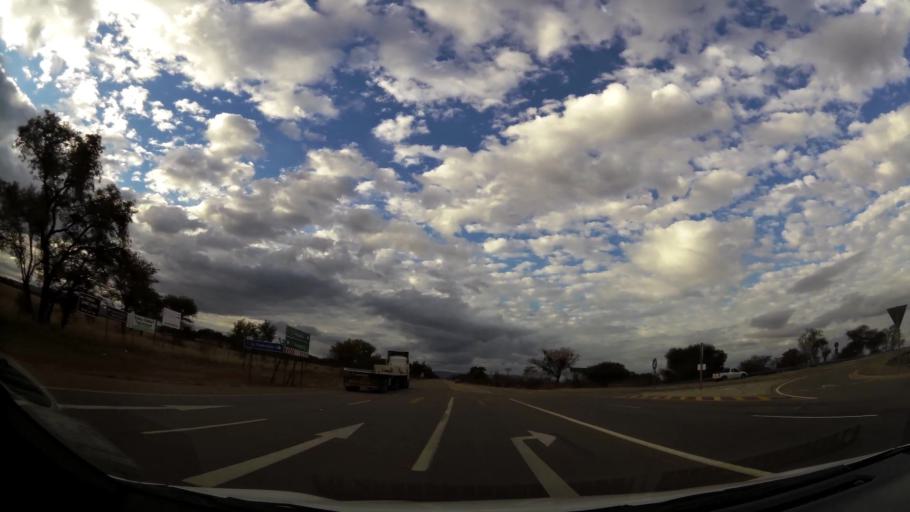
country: ZA
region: Limpopo
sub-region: Waterberg District Municipality
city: Modimolle
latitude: -24.5025
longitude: 28.7307
